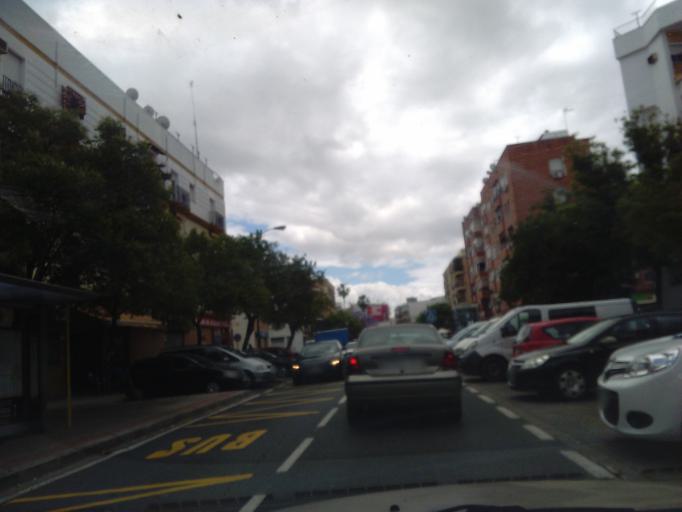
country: ES
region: Andalusia
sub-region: Provincia de Sevilla
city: Sevilla
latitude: 37.3723
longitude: -5.9523
